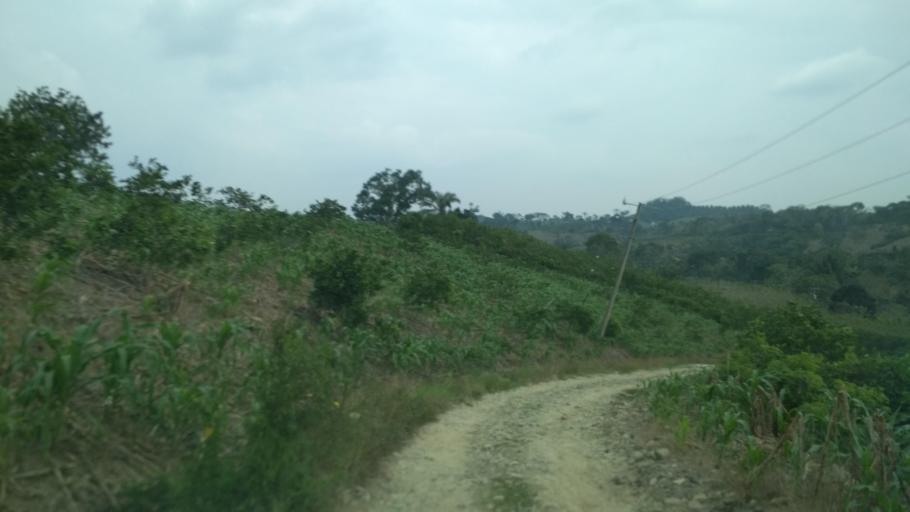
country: MM
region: Kayah
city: Loikaw
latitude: 20.2024
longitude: 97.3021
